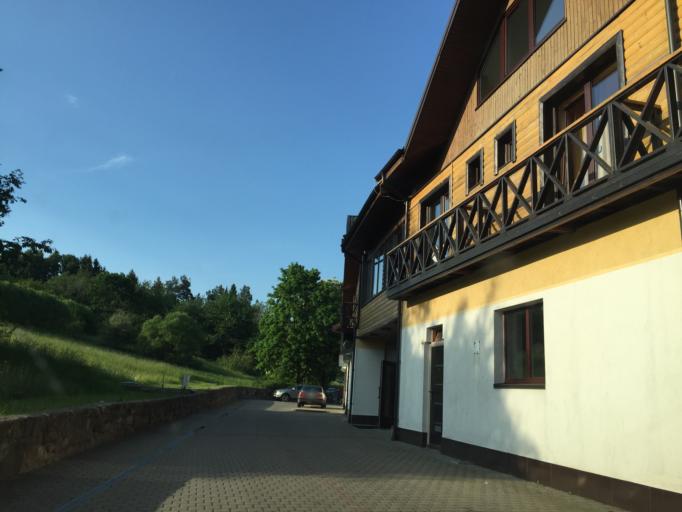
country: LT
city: Plateliai
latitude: 56.0466
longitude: 21.8308
